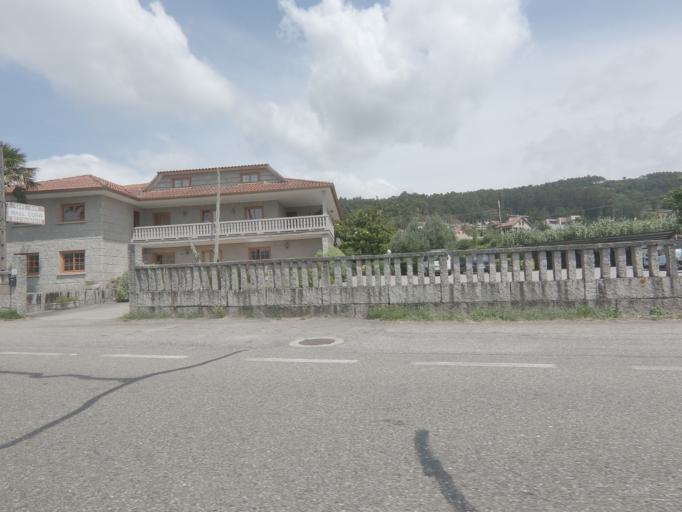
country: ES
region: Galicia
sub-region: Provincia de Pontevedra
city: Tomino
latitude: 42.0352
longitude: -8.7289
